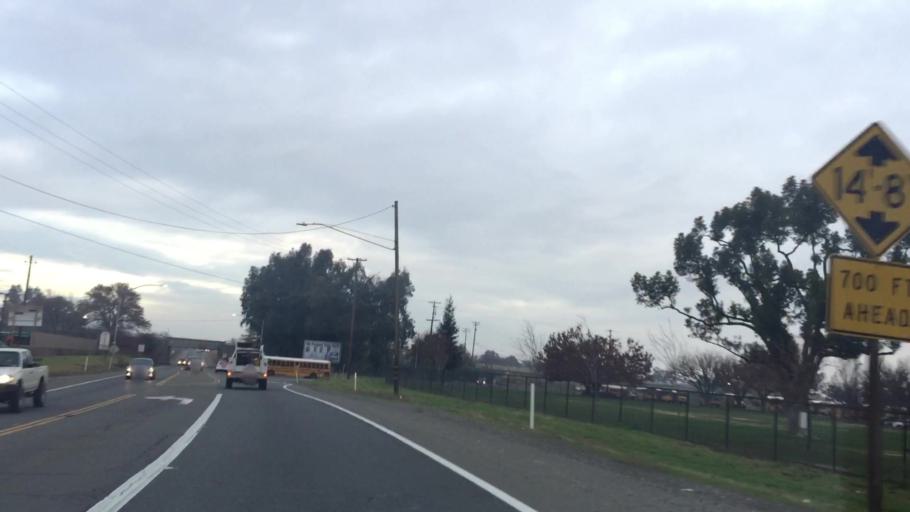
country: US
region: California
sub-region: Yuba County
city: Marysville
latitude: 39.1566
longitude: -121.5884
